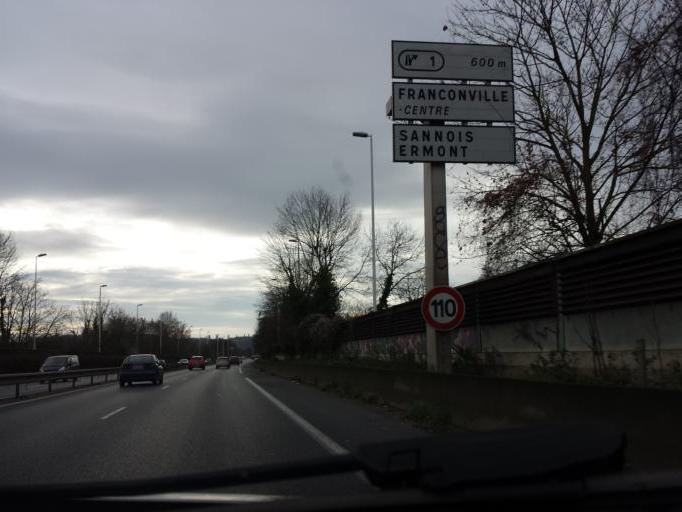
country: FR
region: Ile-de-France
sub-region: Departement du Val-d'Oise
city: Ermont
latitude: 48.9929
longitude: 2.2456
